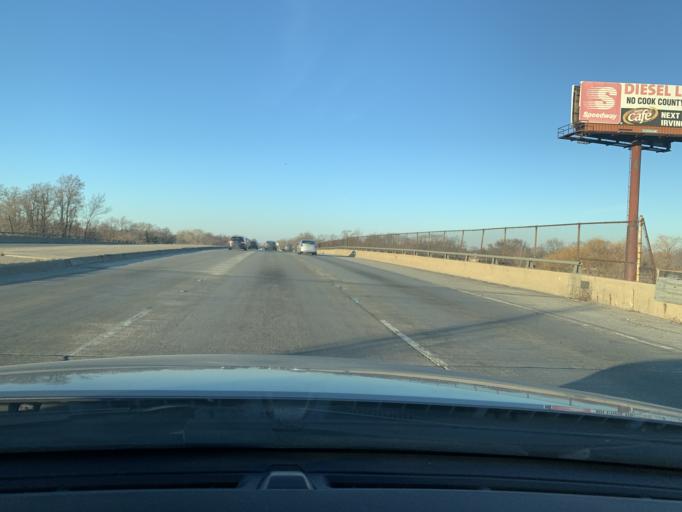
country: US
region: Illinois
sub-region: DuPage County
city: Bensenville
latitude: 41.9594
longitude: -87.9592
